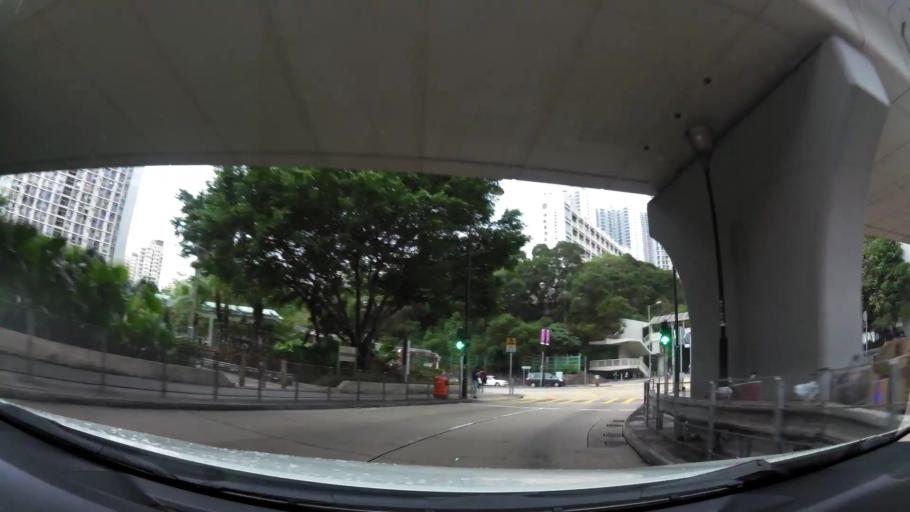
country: HK
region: Tsuen Wan
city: Tsuen Wan
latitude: 22.3618
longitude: 114.1313
